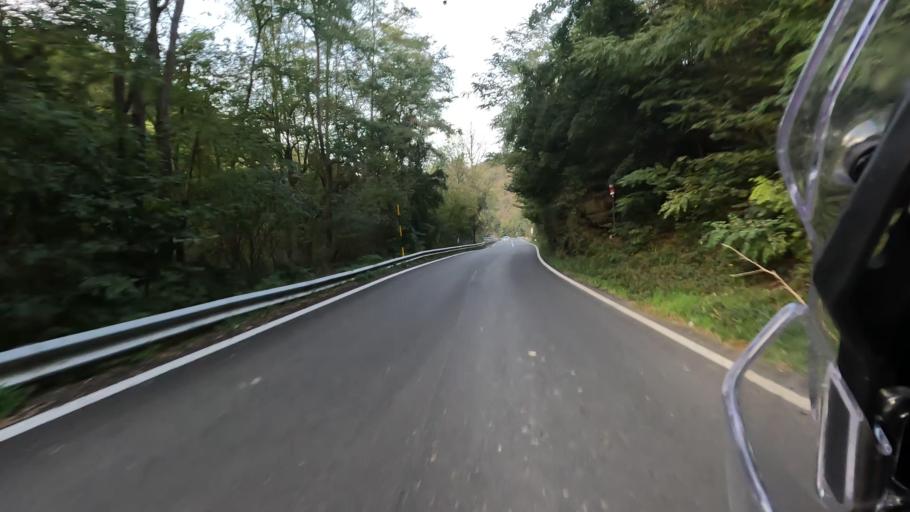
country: IT
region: Liguria
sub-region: Provincia di Savona
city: Osteria dei Cacciatori-Stella
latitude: 44.4494
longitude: 8.4774
